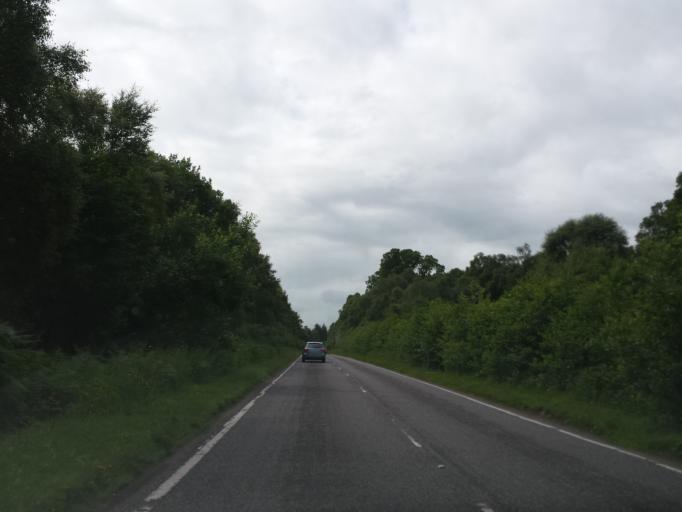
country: GB
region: Scotland
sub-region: Highland
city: Fort William
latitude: 56.8532
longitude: -5.1773
